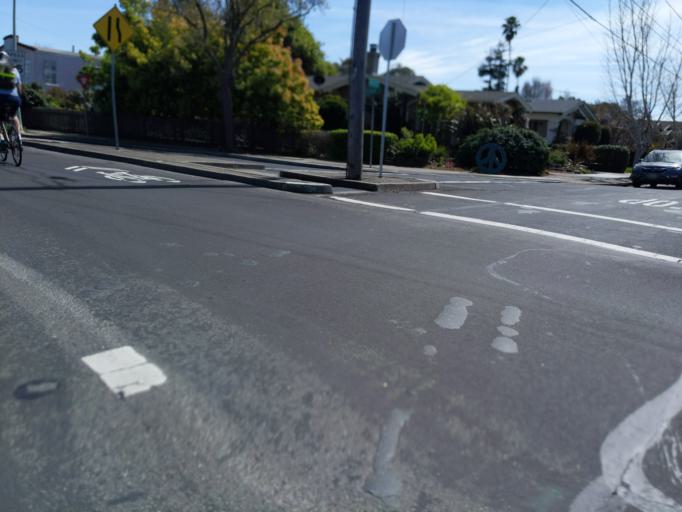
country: US
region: California
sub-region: Alameda County
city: Alameda
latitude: 37.7675
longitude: -122.2331
